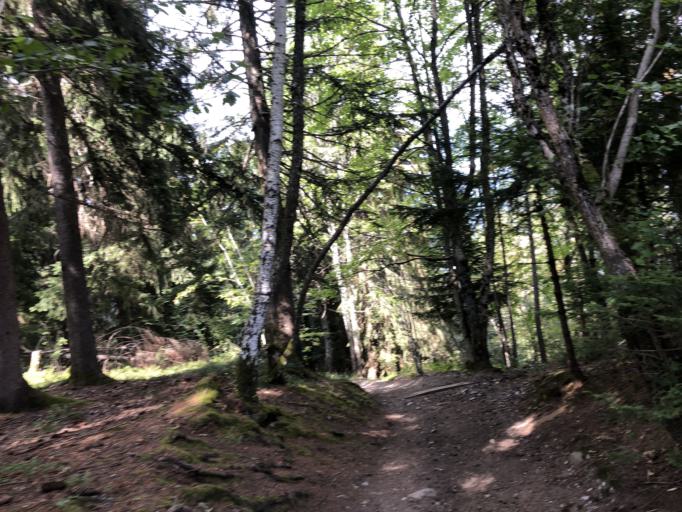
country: FR
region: Rhone-Alpes
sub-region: Departement de la Haute-Savoie
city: Combloux
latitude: 45.8946
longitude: 6.6276
